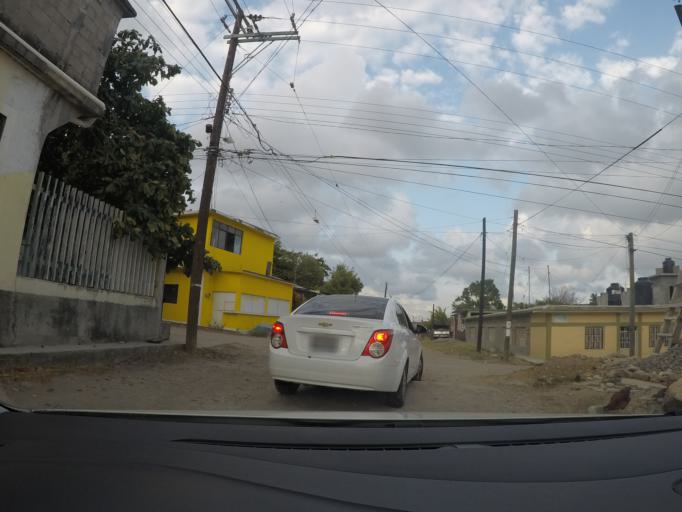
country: MX
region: Oaxaca
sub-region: Salina Cruz
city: Salina Cruz
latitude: 16.2116
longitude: -95.1984
